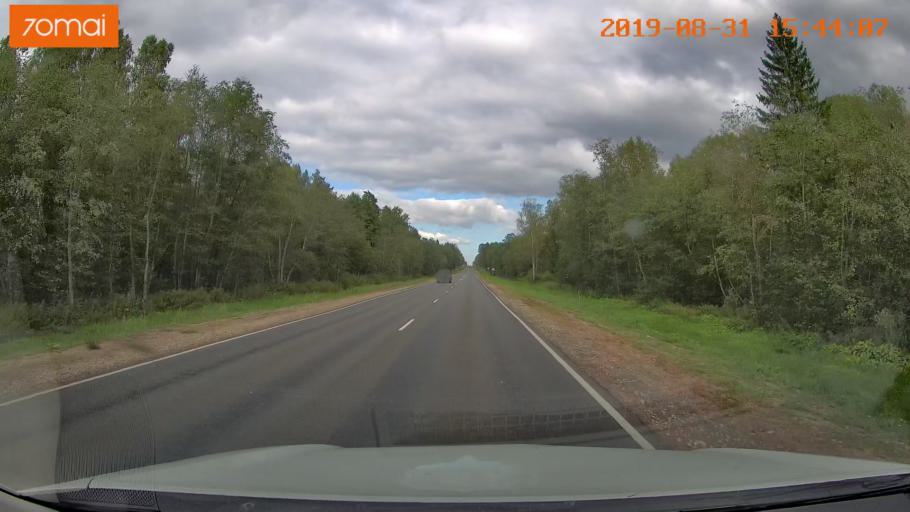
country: RU
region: Kaluga
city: Mosal'sk
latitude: 54.6569
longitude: 34.9250
